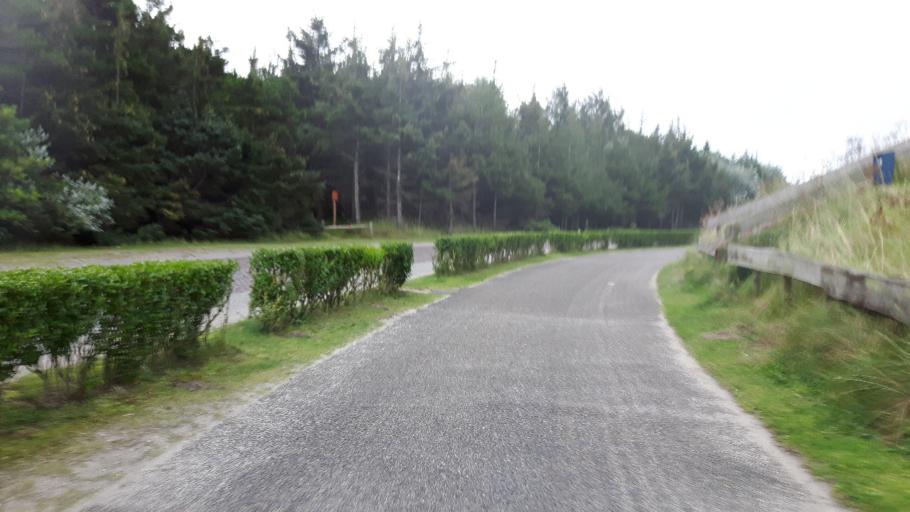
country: NL
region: Friesland
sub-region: Gemeente Ameland
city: Nes
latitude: 53.4563
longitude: 5.7776
